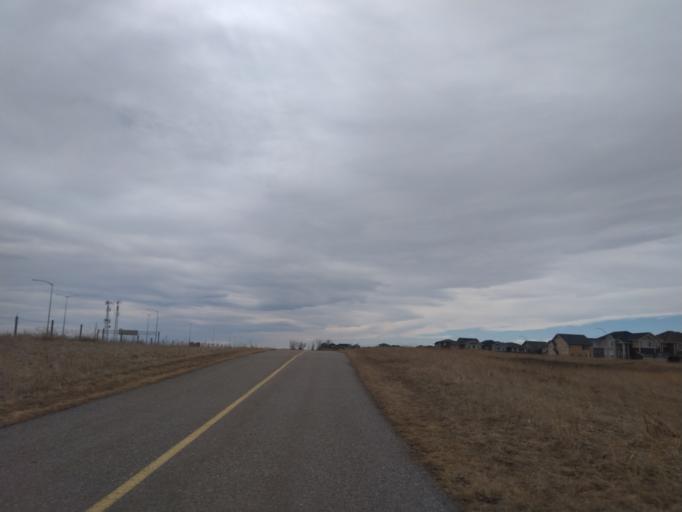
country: CA
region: Alberta
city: Chestermere
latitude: 51.1308
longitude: -113.9227
